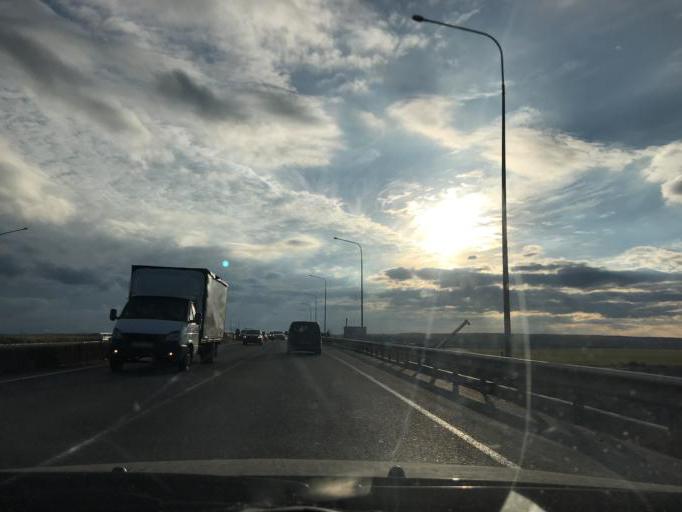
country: RU
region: Kaluga
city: Kurovskoye
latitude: 54.5615
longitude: 36.0426
